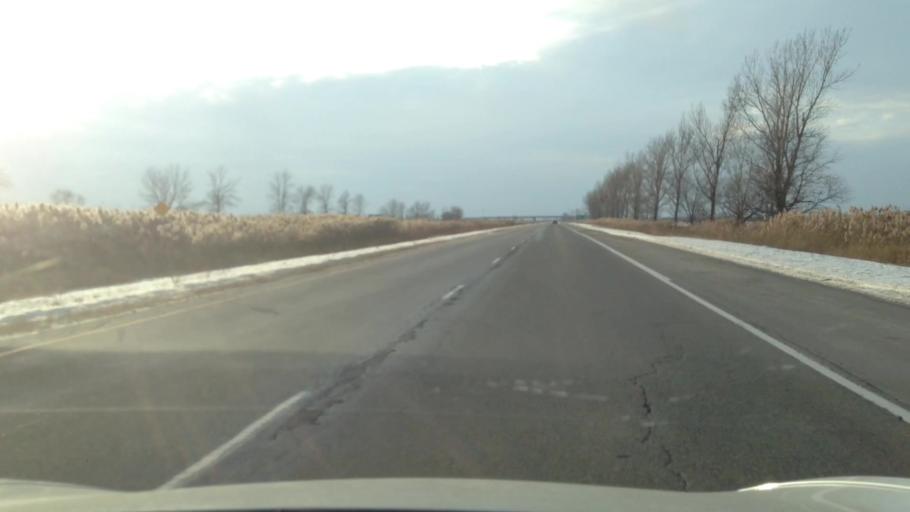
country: CA
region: Ontario
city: Casselman
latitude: 45.3285
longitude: -74.9717
